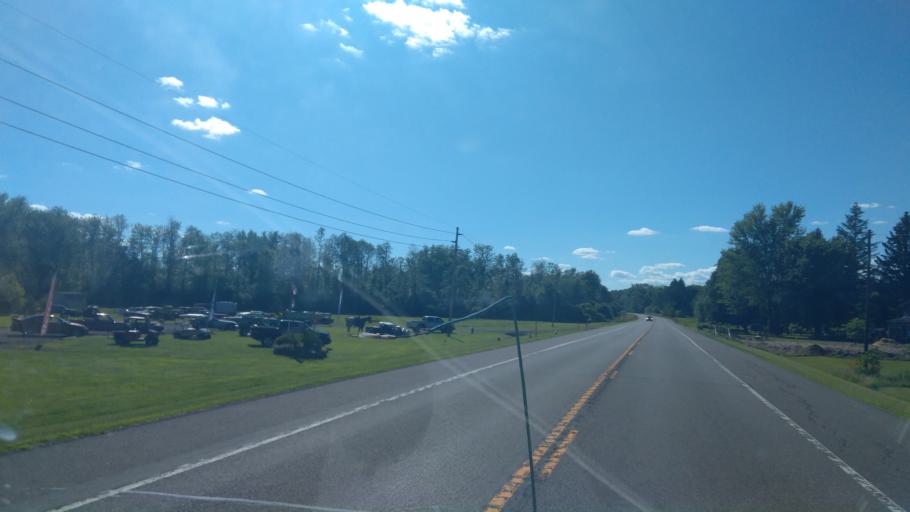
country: US
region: New York
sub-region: Seneca County
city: Seneca Falls
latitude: 42.9572
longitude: -76.8201
